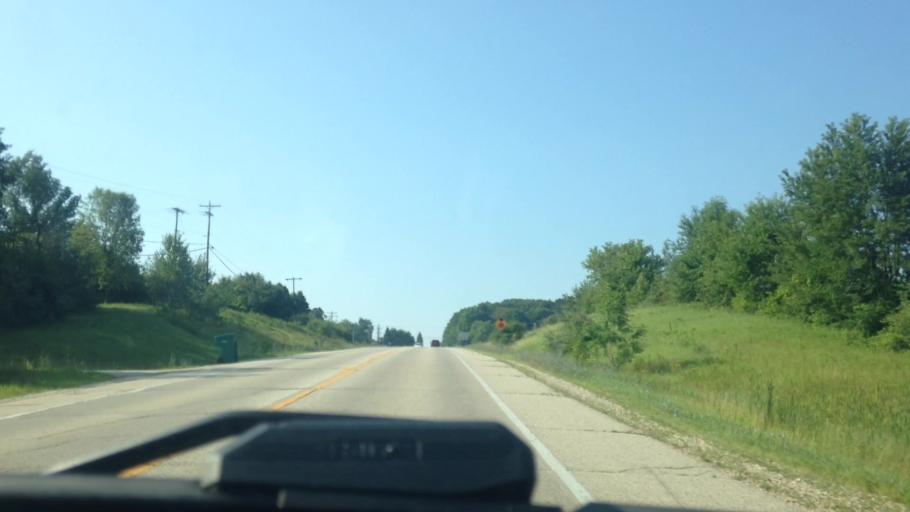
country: US
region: Wisconsin
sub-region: Washington County
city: Richfield
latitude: 43.2548
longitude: -88.2618
